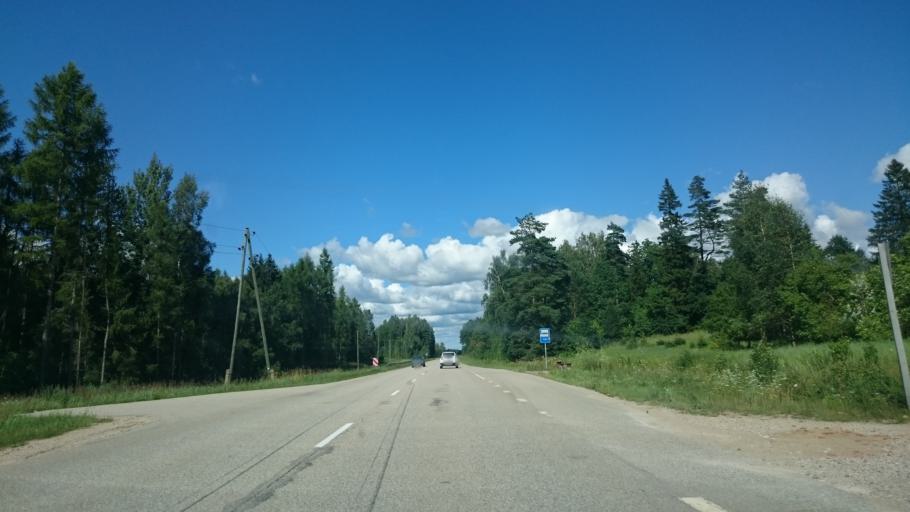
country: LV
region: Kuldigas Rajons
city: Kuldiga
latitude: 56.8862
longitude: 21.8801
